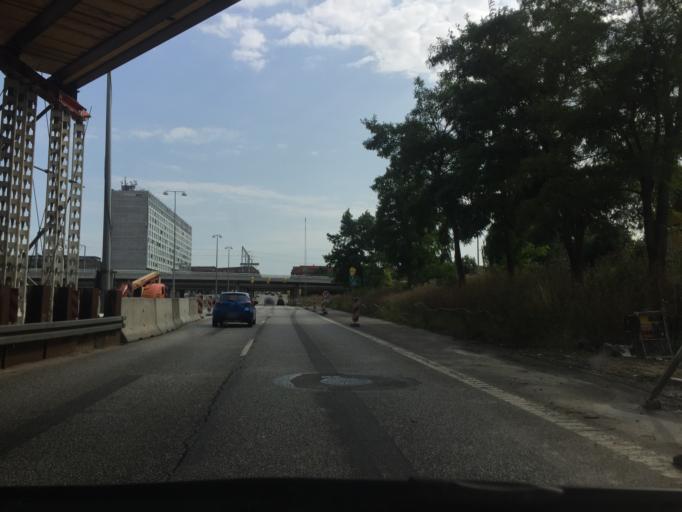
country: DK
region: Capital Region
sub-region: Kobenhavn
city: Copenhagen
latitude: 55.7163
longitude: 12.5579
